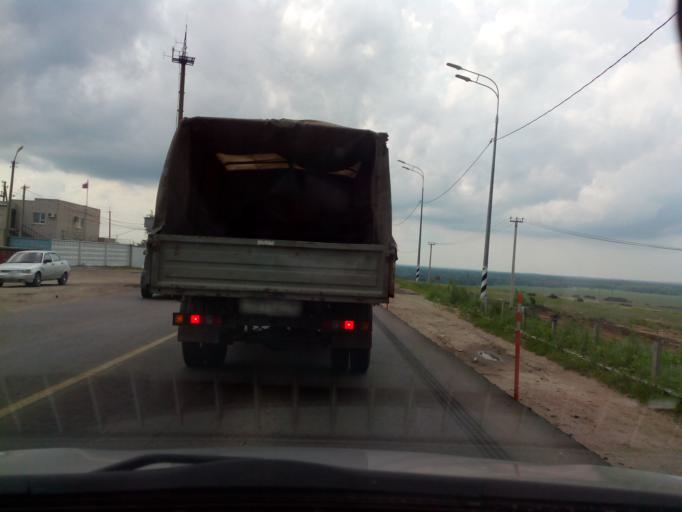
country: RU
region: Volgograd
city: Mikhaylovka
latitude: 50.0270
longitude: 43.1896
